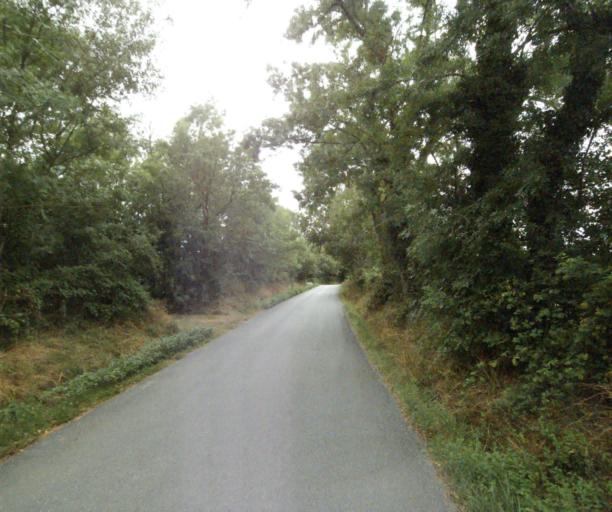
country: FR
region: Midi-Pyrenees
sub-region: Departement du Tarn
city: Soreze
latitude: 43.4575
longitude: 2.0603
